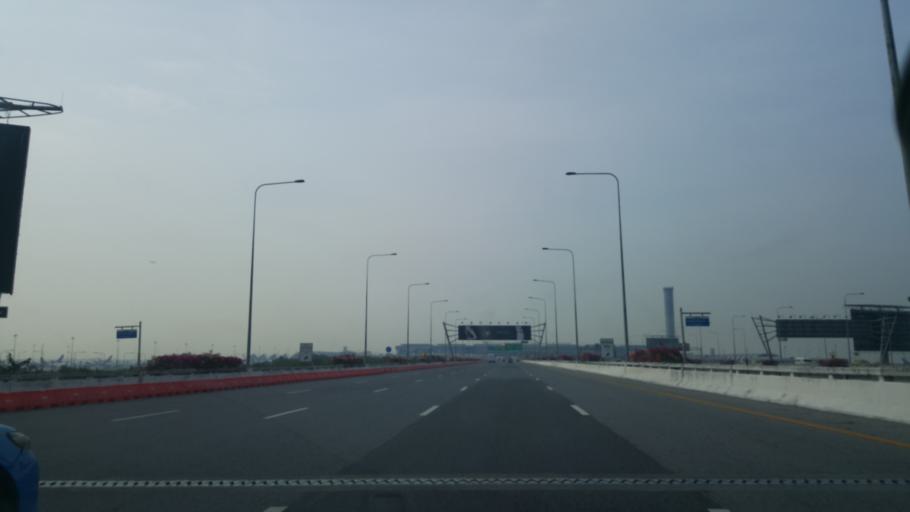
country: TH
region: Bangkok
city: Lat Krabang
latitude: 13.7062
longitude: 100.7546
